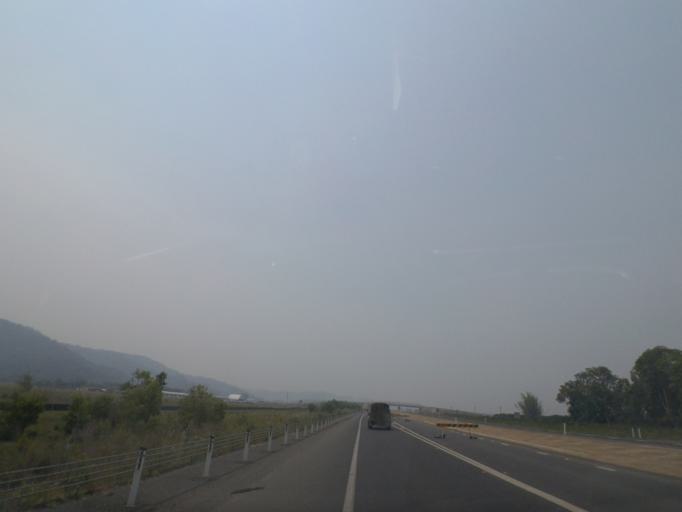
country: AU
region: New South Wales
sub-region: Ballina
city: Ballina
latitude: -28.9064
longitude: 153.4789
